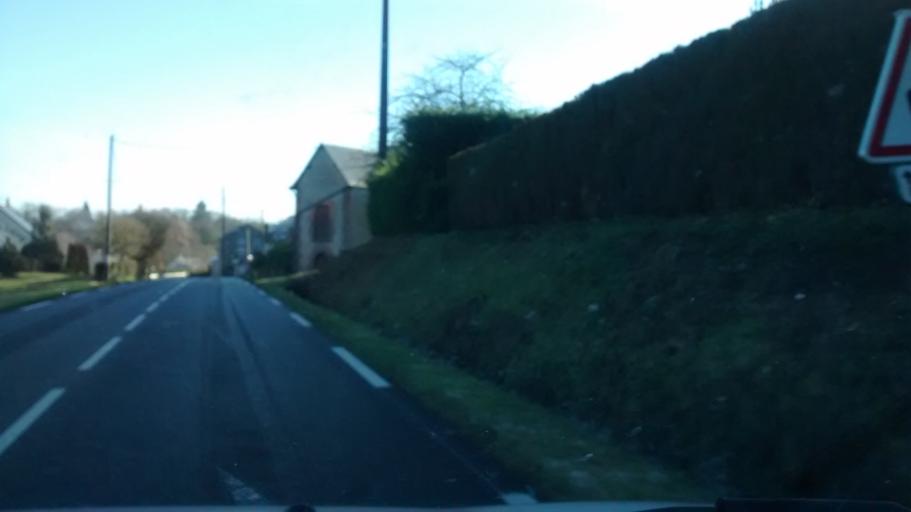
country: FR
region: Centre
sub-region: Departement d'Indre-et-Loire
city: Reugny
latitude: 47.4848
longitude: 0.8580
